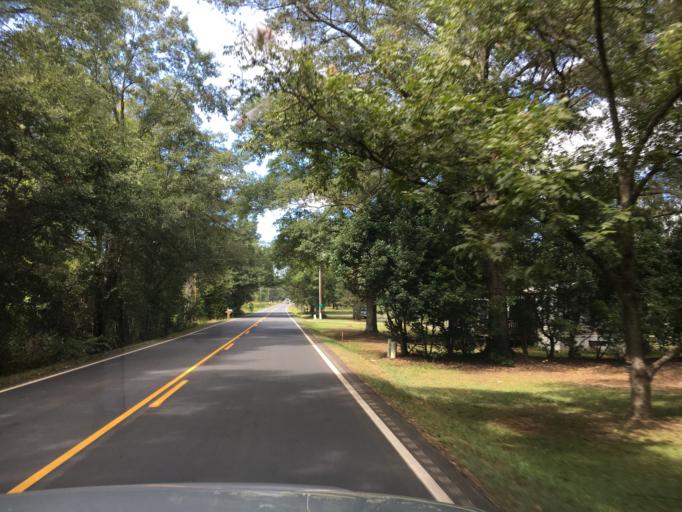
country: US
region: South Carolina
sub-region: Spartanburg County
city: Duncan
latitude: 34.9484
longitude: -82.1428
